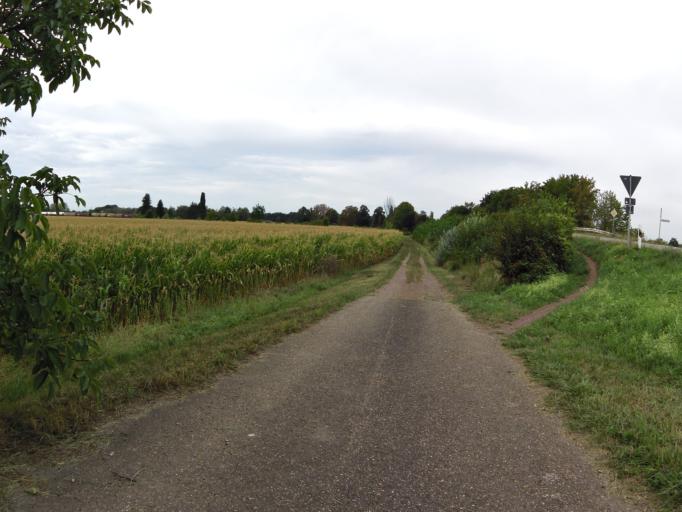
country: DE
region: Baden-Wuerttemberg
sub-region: Freiburg Region
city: Lahr
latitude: 48.3572
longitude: 7.8496
